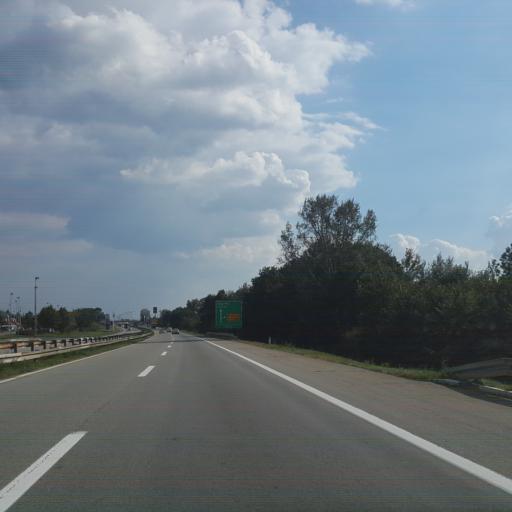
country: RS
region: Central Serbia
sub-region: Podunavski Okrug
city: Velika Plana
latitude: 44.3519
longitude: 21.0740
